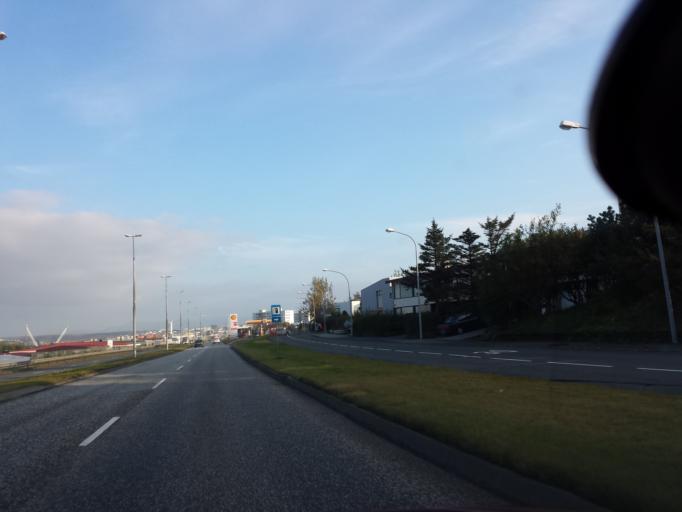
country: IS
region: Capital Region
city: Reykjavik
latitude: 64.1473
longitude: -21.8614
